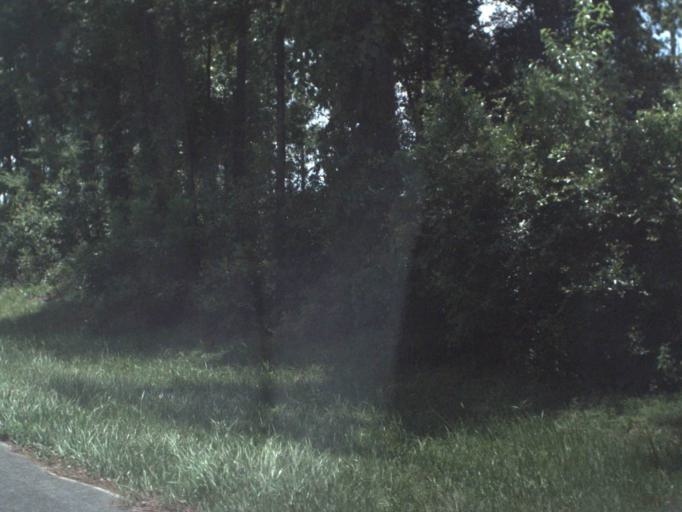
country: US
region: Florida
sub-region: Alachua County
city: Archer
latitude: 29.4624
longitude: -82.4779
